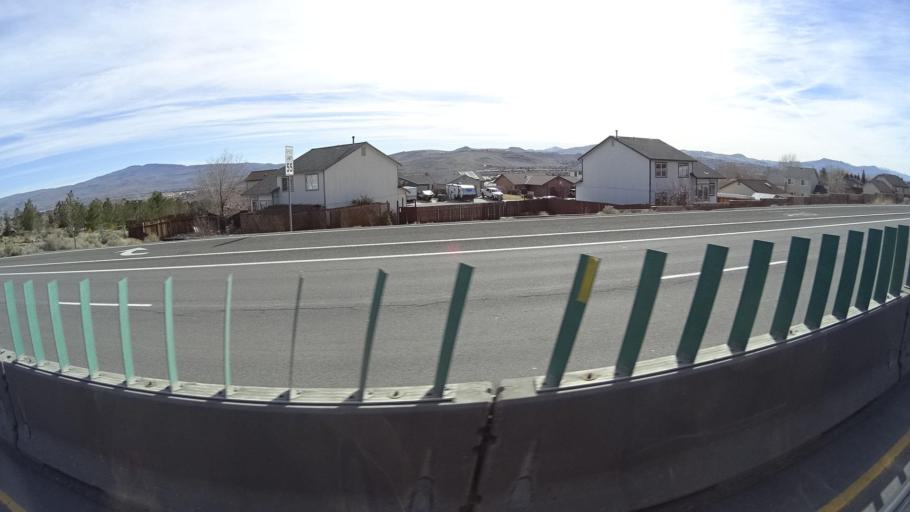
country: US
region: Nevada
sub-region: Washoe County
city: Sun Valley
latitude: 39.6022
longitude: -119.7344
